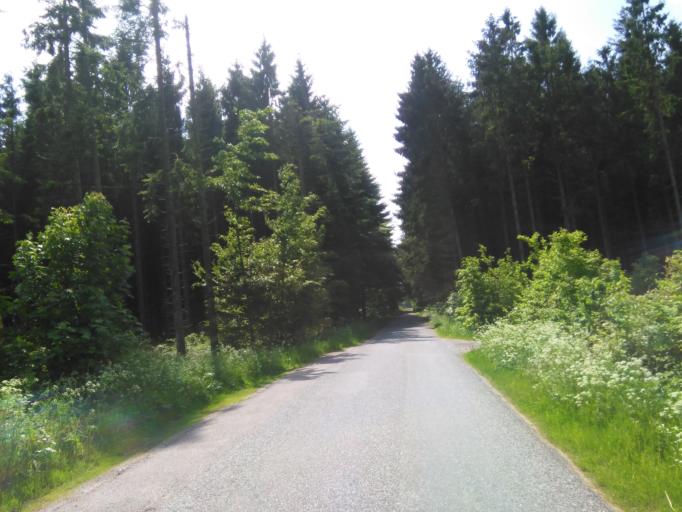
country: DK
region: Central Jutland
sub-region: Arhus Kommune
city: Sabro
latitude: 56.2745
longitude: 9.9790
